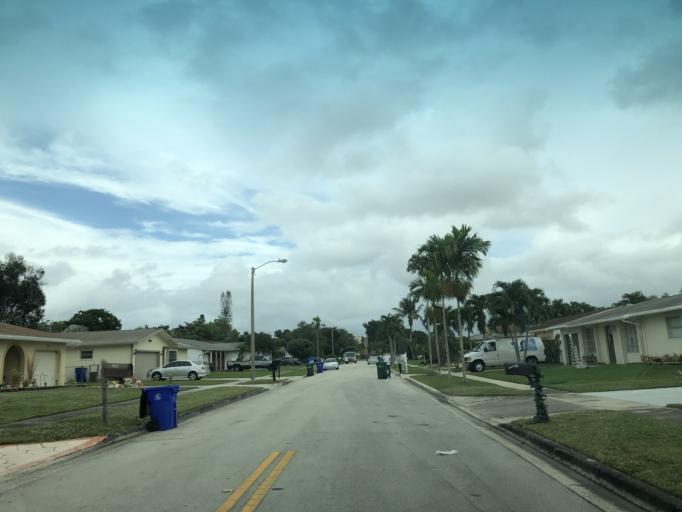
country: US
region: Florida
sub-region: Broward County
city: North Lauderdale
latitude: 26.2410
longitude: -80.2331
